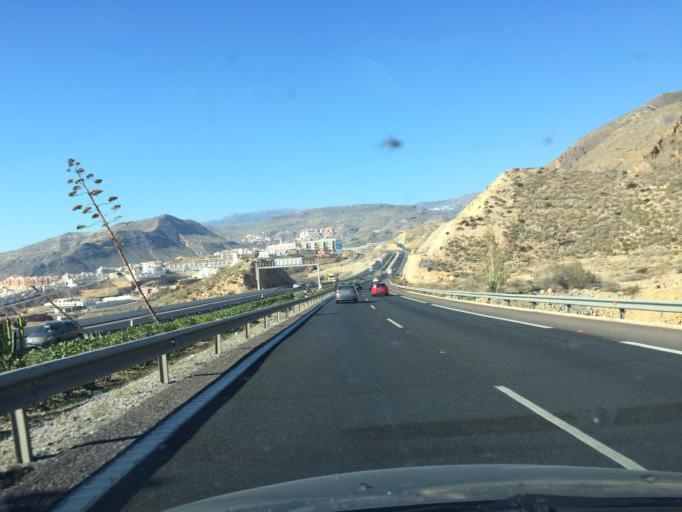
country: ES
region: Andalusia
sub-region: Provincia de Almeria
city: Aguadulce
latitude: 36.8227
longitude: -2.5744
